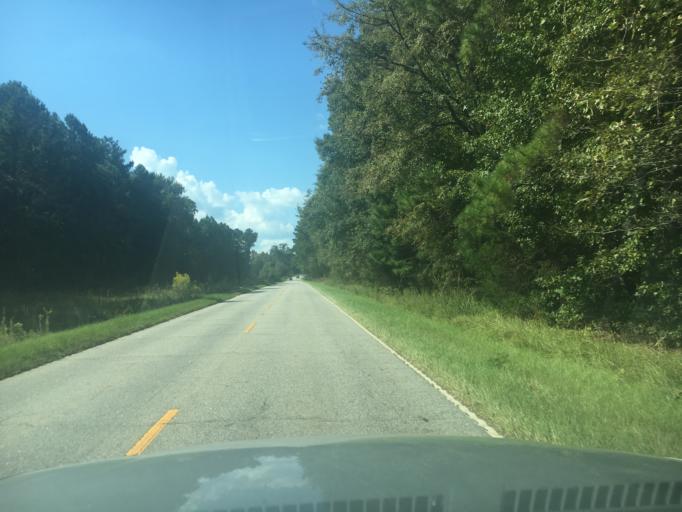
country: US
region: South Carolina
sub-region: Greenwood County
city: Greenwood
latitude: 34.2670
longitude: -82.1883
